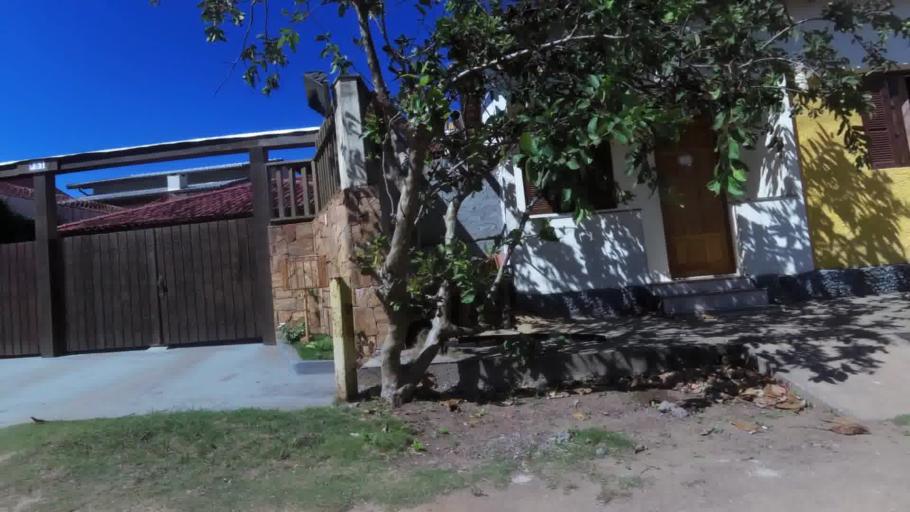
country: BR
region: Espirito Santo
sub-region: Guarapari
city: Guarapari
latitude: -20.7419
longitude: -40.5364
